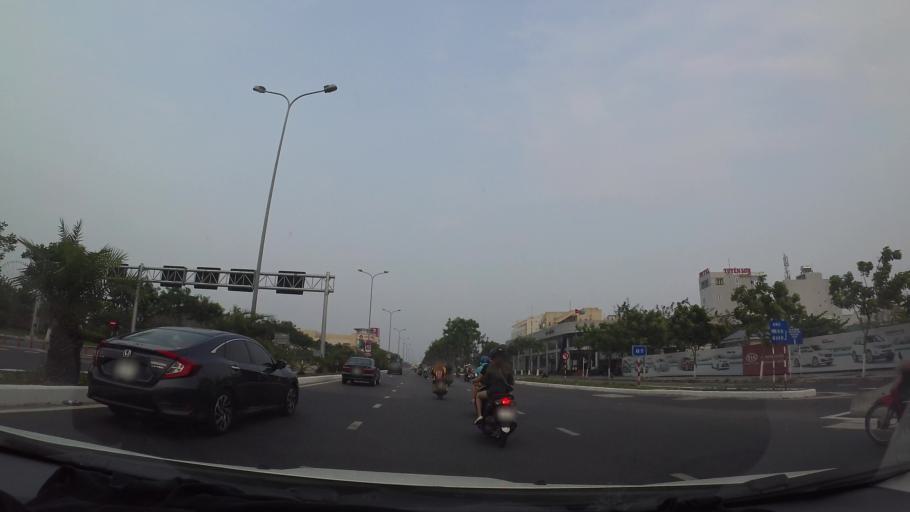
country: VN
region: Da Nang
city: Cam Le
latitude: 16.0331
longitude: 108.2248
